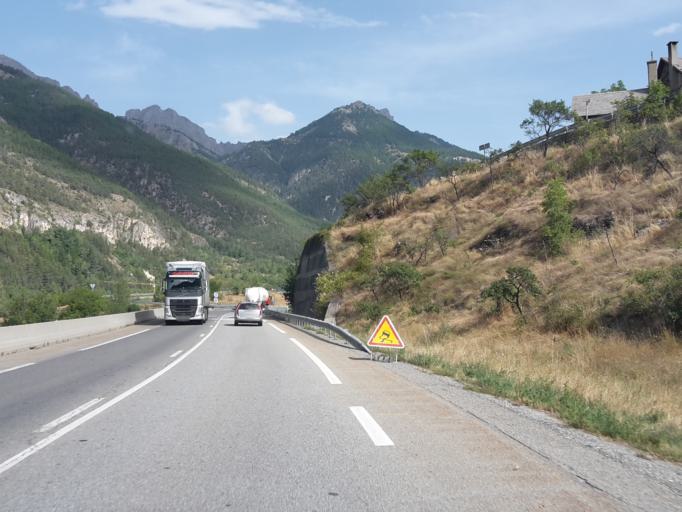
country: FR
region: Provence-Alpes-Cote d'Azur
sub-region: Departement des Hautes-Alpes
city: Saint-Martin-de-Queyrieres
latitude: 44.8417
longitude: 6.5838
